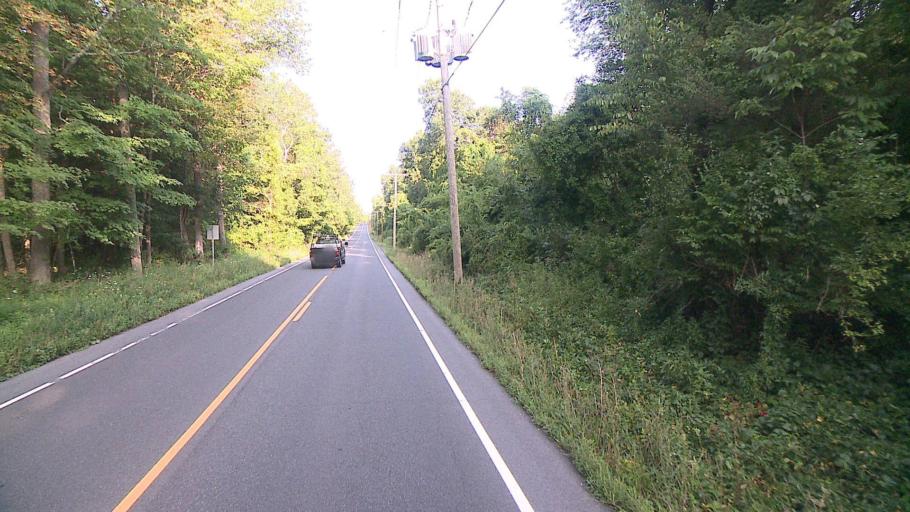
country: US
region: Connecticut
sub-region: Litchfield County
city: Kent
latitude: 41.6637
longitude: -73.4961
